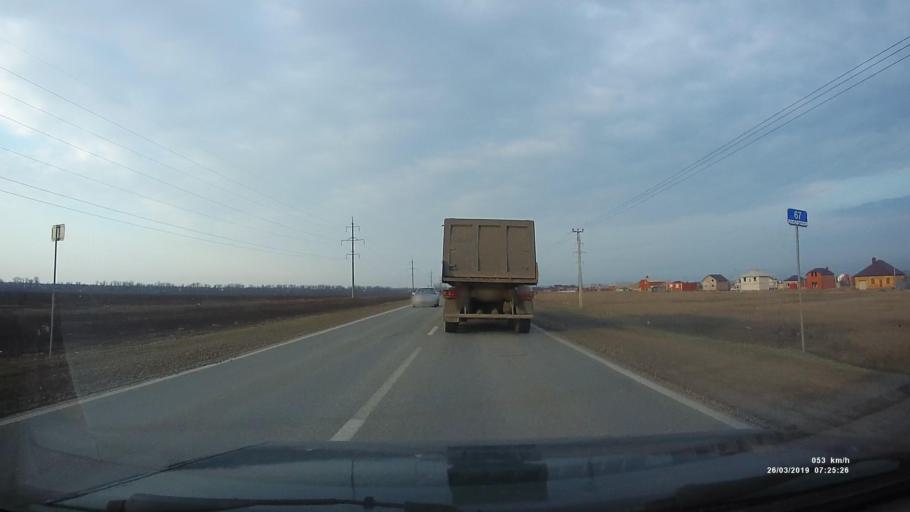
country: RU
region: Rostov
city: Taganrog
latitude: 47.2715
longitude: 38.8489
